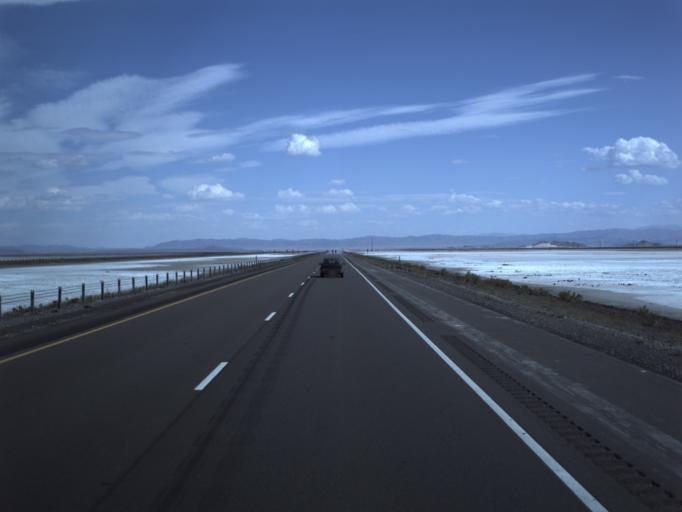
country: US
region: Utah
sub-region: Tooele County
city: Wendover
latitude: 40.7286
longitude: -113.4010
